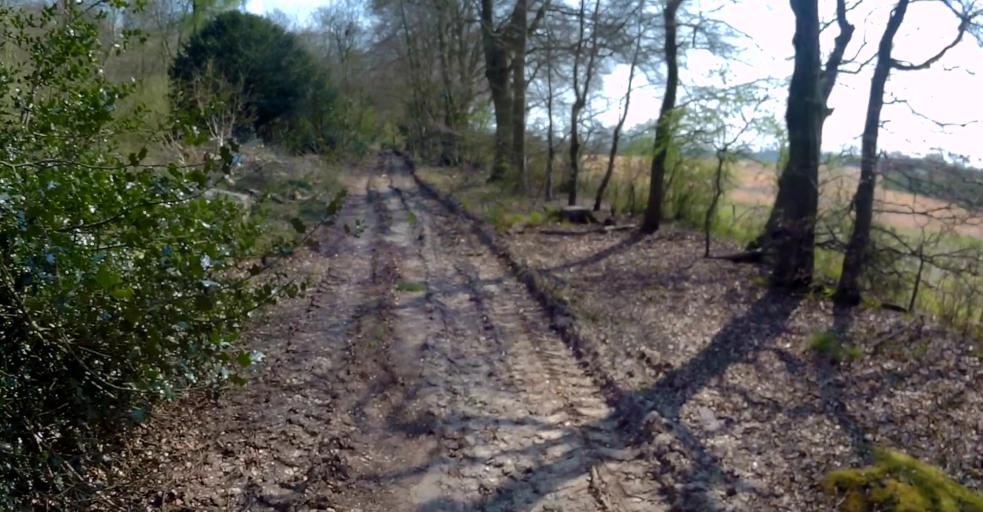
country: GB
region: England
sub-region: Hampshire
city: Overton
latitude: 51.1851
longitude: -1.2440
